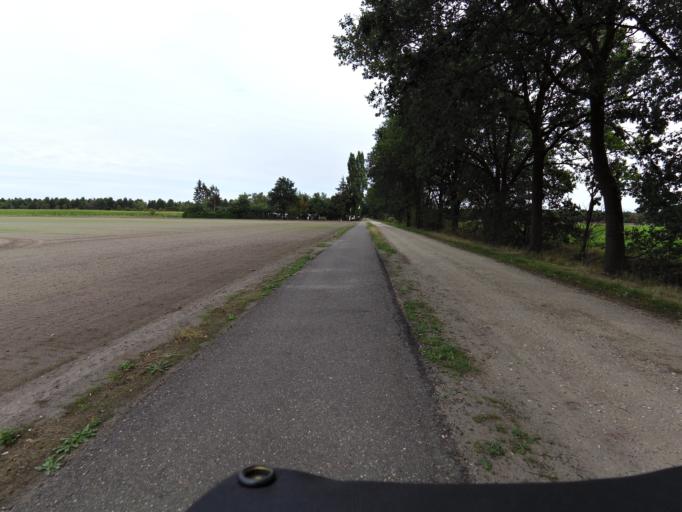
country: NL
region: Limburg
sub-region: Gemeente Bergen
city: Wellerlooi
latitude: 51.5790
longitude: 6.1143
